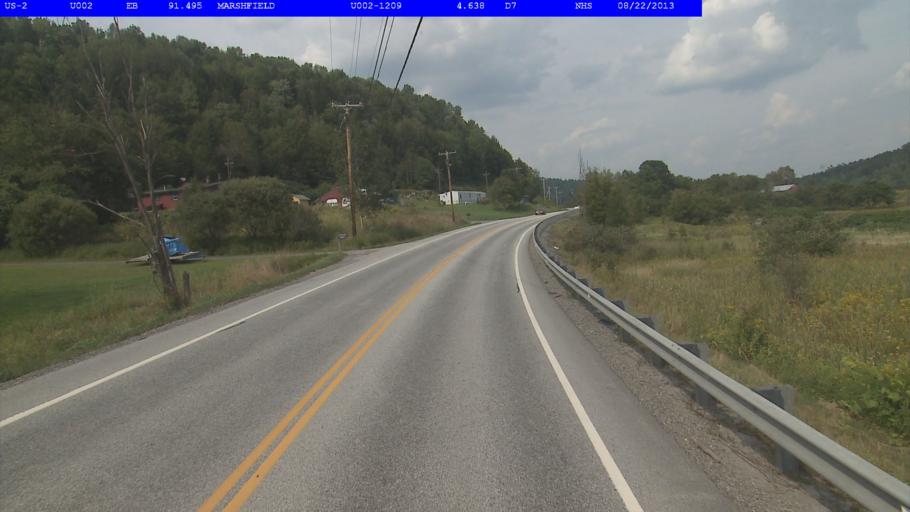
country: US
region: Vermont
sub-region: Caledonia County
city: Hardwick
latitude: 44.3314
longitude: -72.3763
